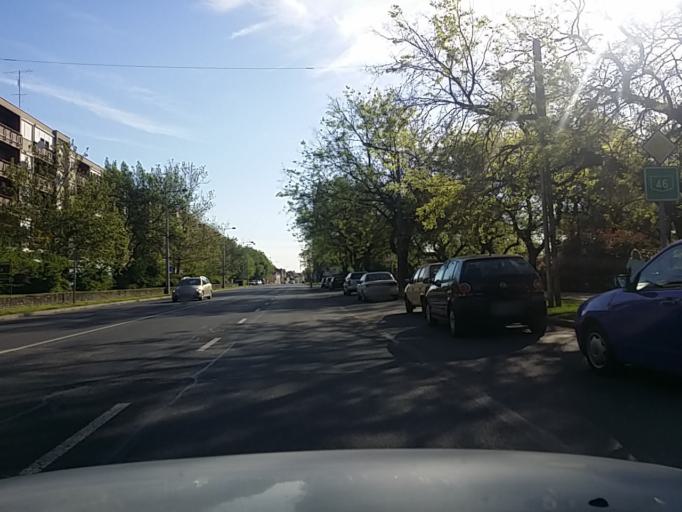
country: HU
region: Jasz-Nagykun-Szolnok
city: Torokszentmiklos
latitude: 47.1793
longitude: 20.4114
